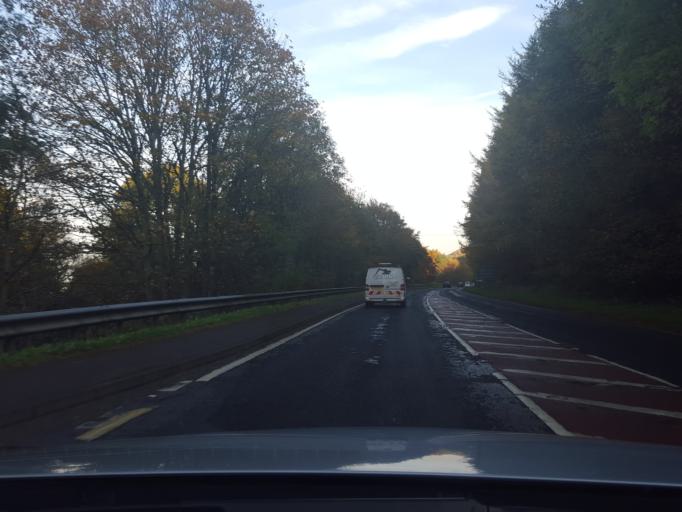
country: GB
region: Scotland
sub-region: Highland
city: Inverness
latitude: 57.4584
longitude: -4.2672
